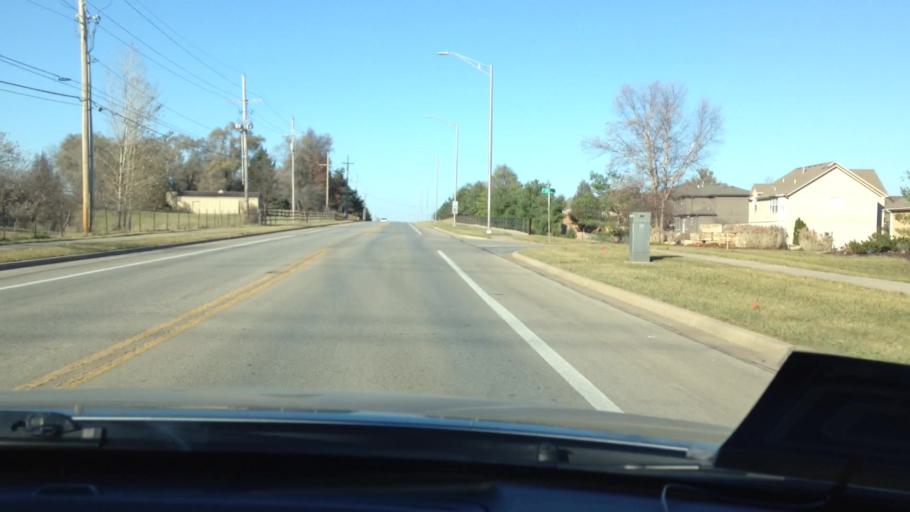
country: US
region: Kansas
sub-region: Johnson County
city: Olathe
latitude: 38.9343
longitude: -94.8161
